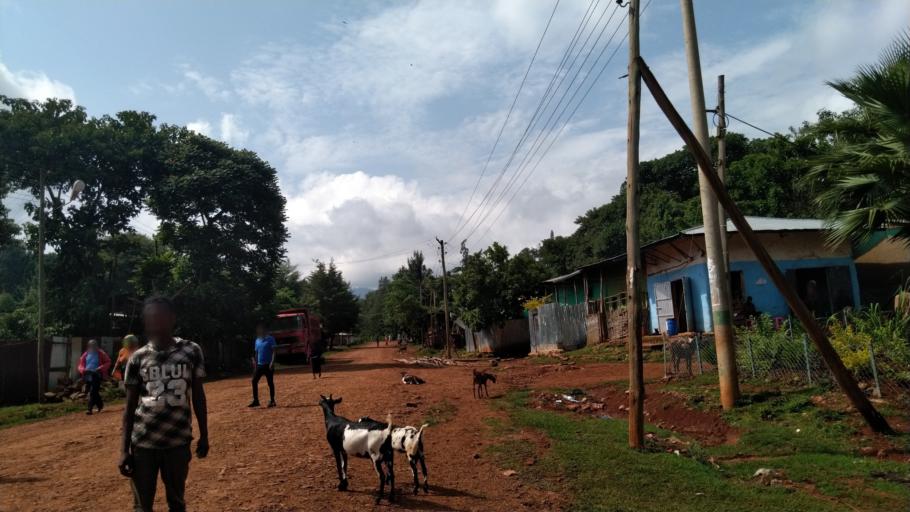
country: ET
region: Oromiya
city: Jima
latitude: 7.6278
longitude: 37.2552
